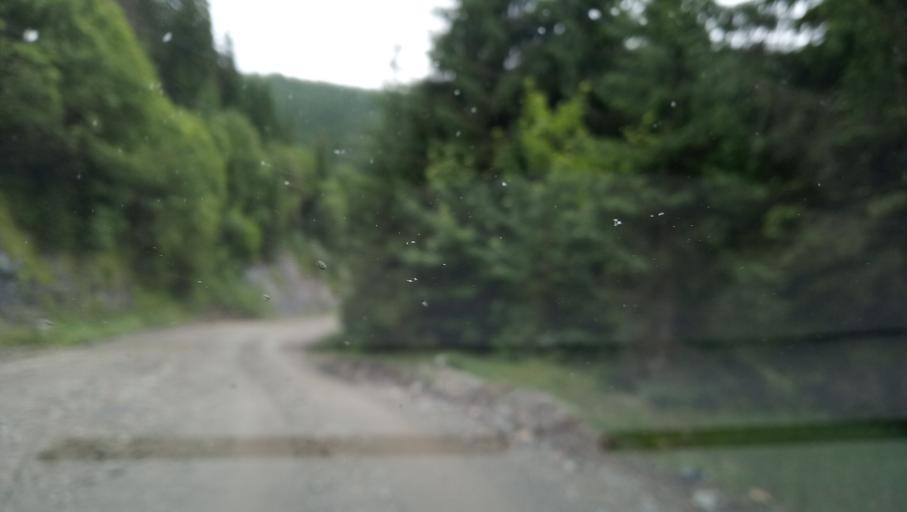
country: RO
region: Hunedoara
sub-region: Oras Petrila
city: Petrila
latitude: 45.4010
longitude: 23.5717
